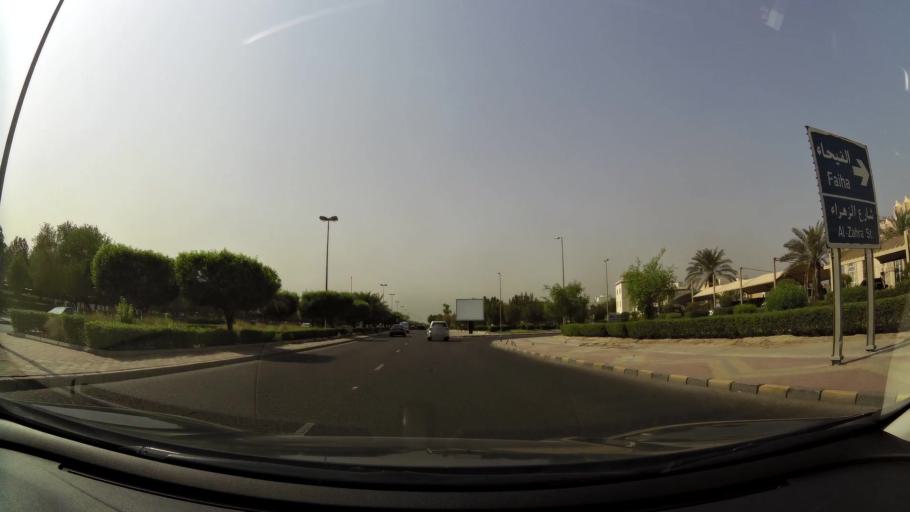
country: KW
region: Al Asimah
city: Ash Shamiyah
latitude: 29.3337
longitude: 47.9826
